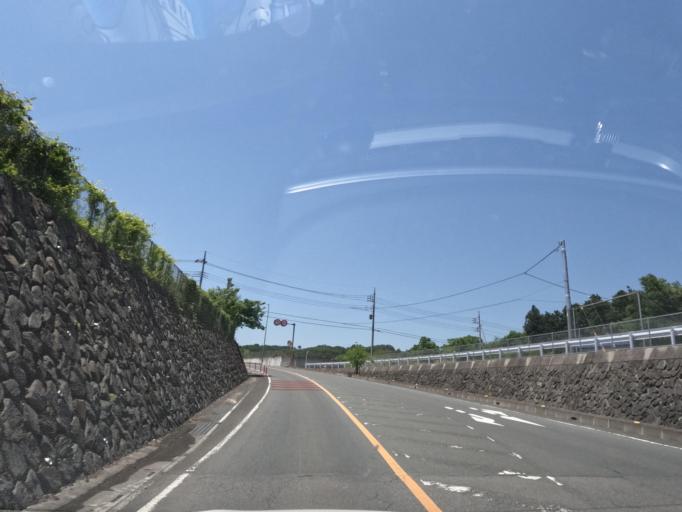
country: JP
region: Saitama
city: Chichibu
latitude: 36.0468
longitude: 139.0928
